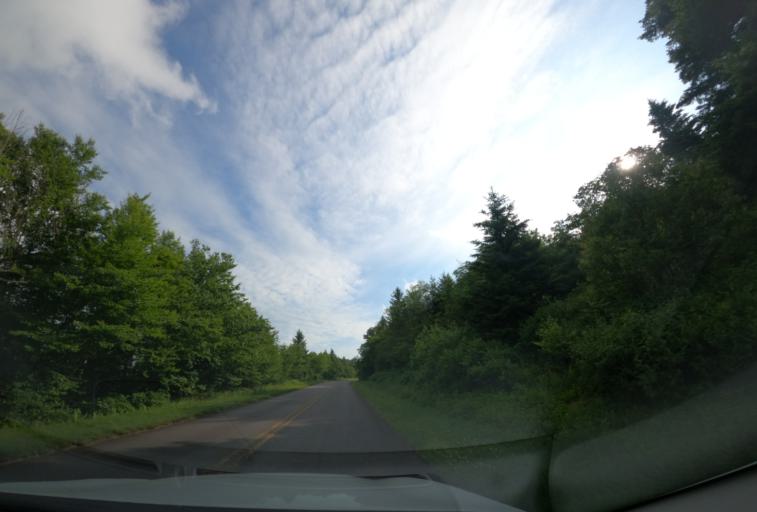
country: US
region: North Carolina
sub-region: Transylvania County
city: Brevard
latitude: 35.3033
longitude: -82.9040
